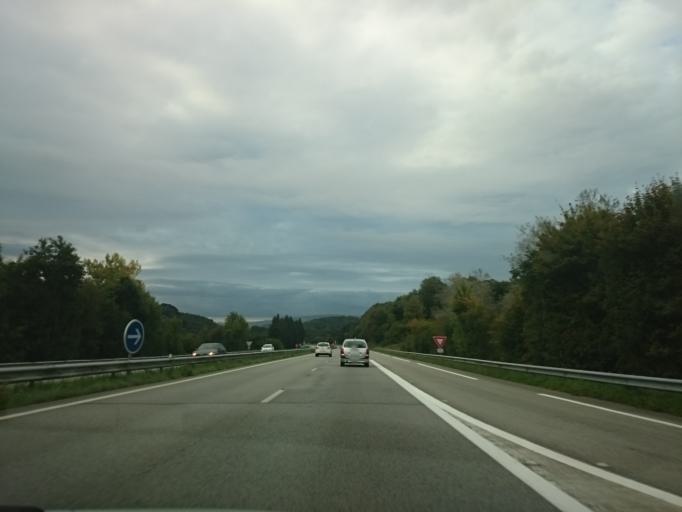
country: FR
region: Brittany
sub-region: Departement du Finistere
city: Dineault
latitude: 48.2580
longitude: -4.1144
